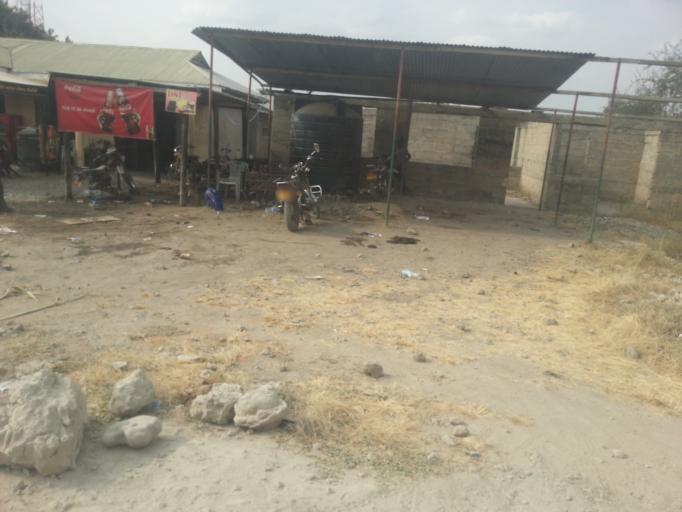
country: TZ
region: Arusha
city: Mto wa Mbu
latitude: -3.6963
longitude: 35.9388
